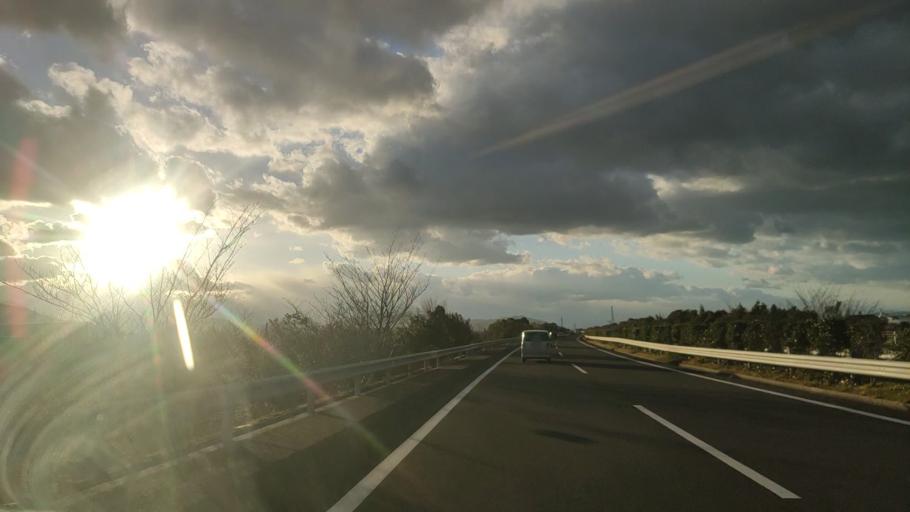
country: JP
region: Ehime
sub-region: Shikoku-chuo Shi
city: Matsuyama
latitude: 33.7858
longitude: 132.8711
